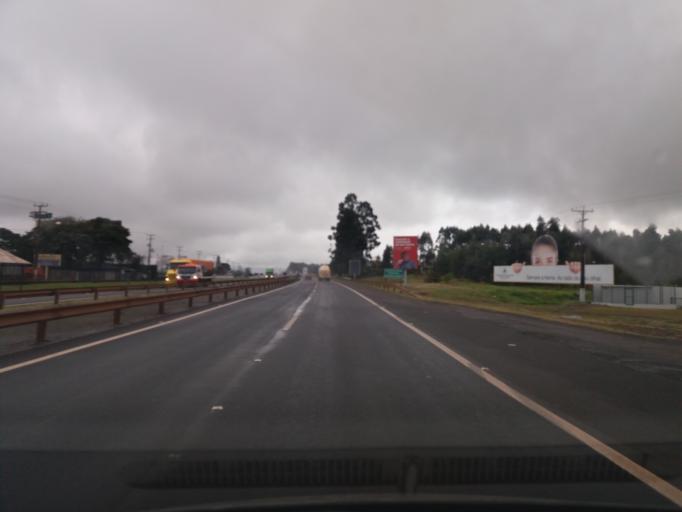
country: BR
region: Parana
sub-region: Cascavel
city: Cascavel
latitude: -24.9964
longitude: -53.5154
